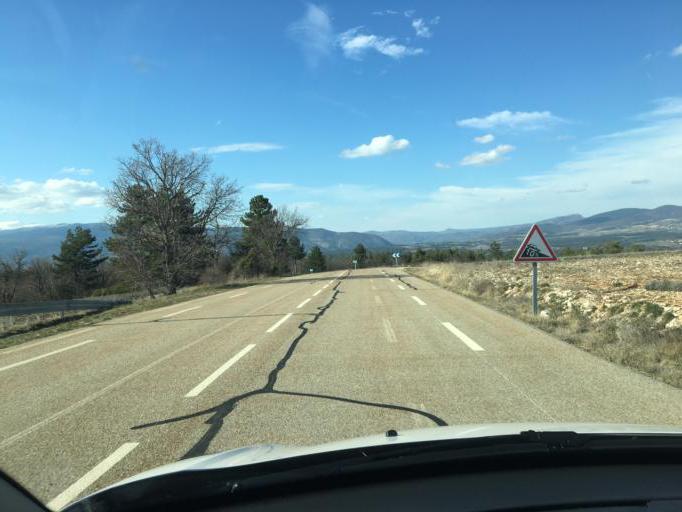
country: FR
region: Provence-Alpes-Cote d'Azur
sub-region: Departement du Vaucluse
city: Sault
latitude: 44.0496
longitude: 5.4418
